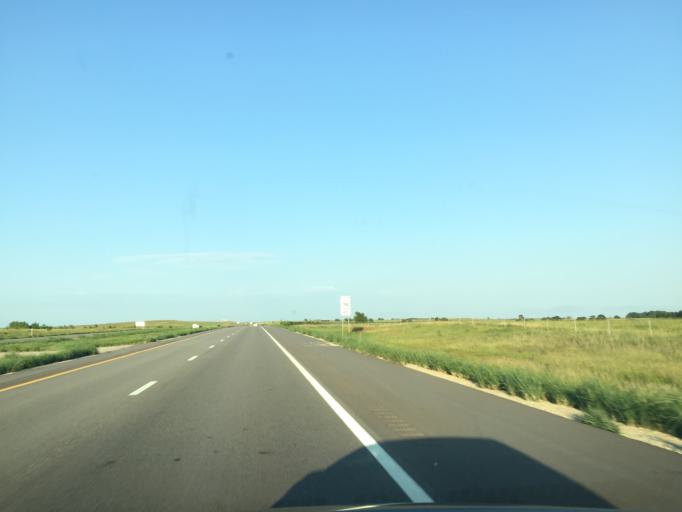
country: US
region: Kansas
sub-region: Russell County
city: Russell
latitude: 38.8569
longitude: -98.5750
